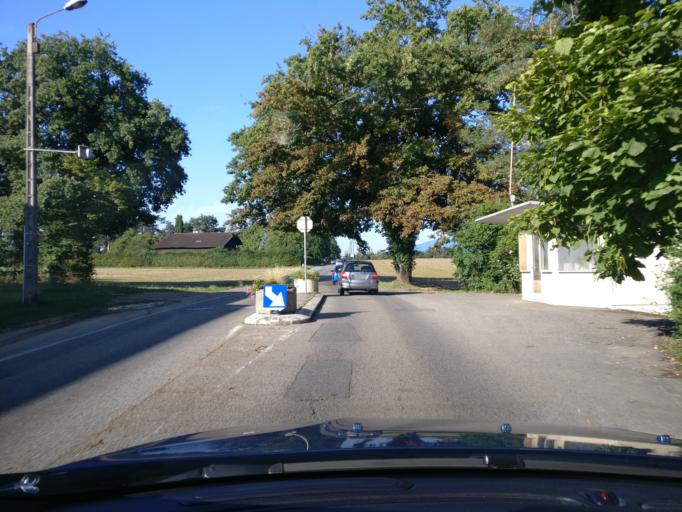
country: CH
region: Geneva
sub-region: Geneva
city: Meyrin
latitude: 46.2445
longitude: 6.0934
